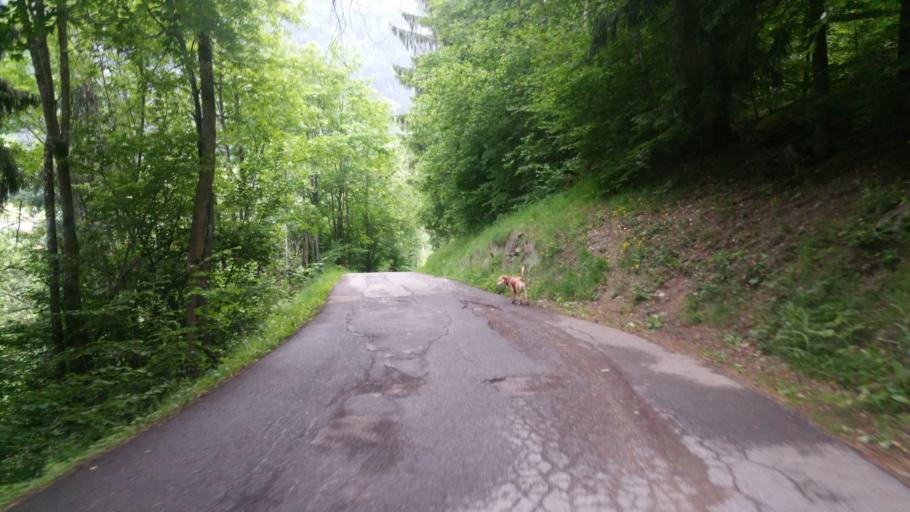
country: FR
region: Rhone-Alpes
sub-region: Departement de la Haute-Savoie
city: Les Houches
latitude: 45.8968
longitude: 6.8000
